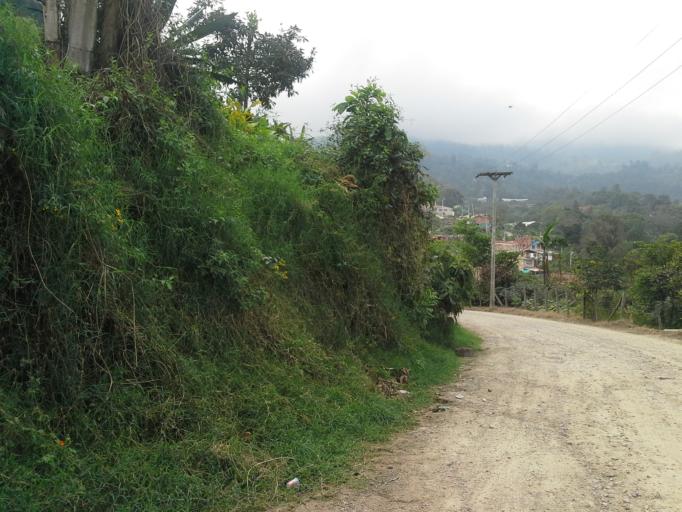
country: CO
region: Cundinamarca
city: San Antonio del Tequendama
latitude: 4.5930
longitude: -74.3390
